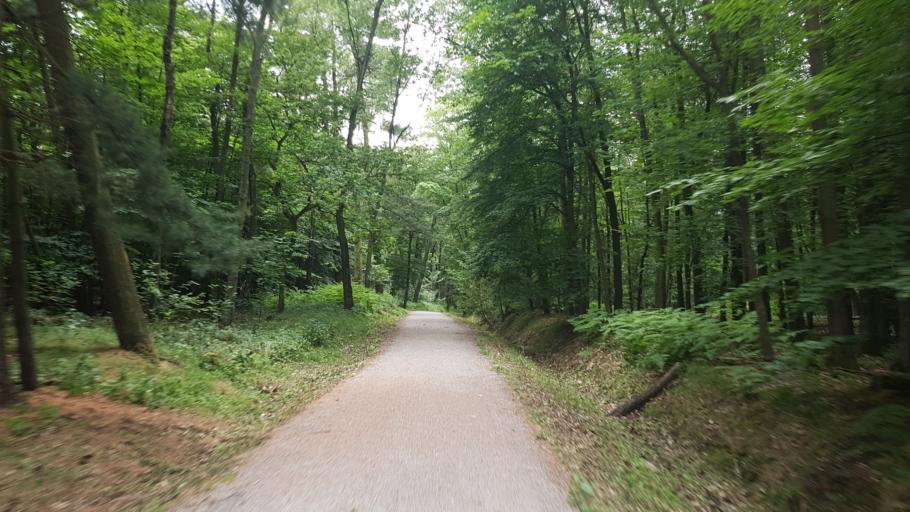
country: DE
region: North Rhine-Westphalia
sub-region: Regierungsbezirk Dusseldorf
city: Muelheim (Ruhr)
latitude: 51.4025
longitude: 6.8275
